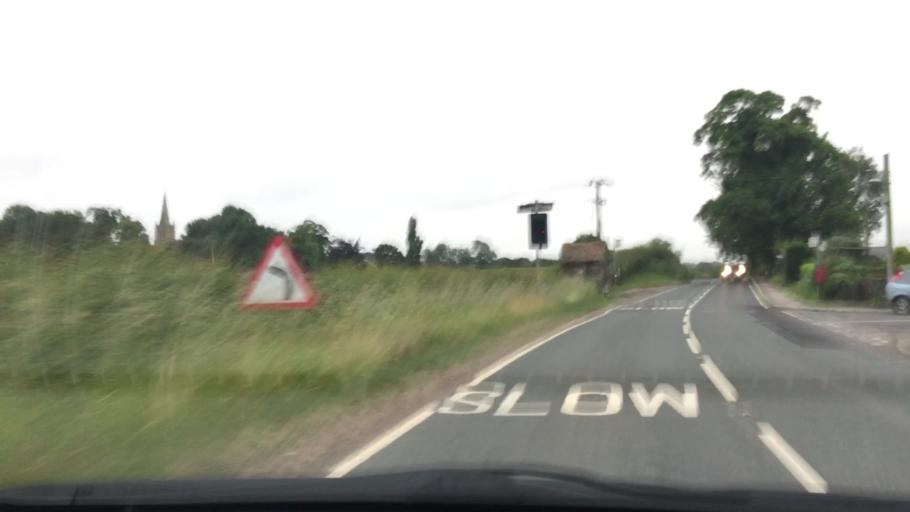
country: GB
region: England
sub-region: City and Borough of Leeds
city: Wetherby
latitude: 53.9518
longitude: -1.3975
